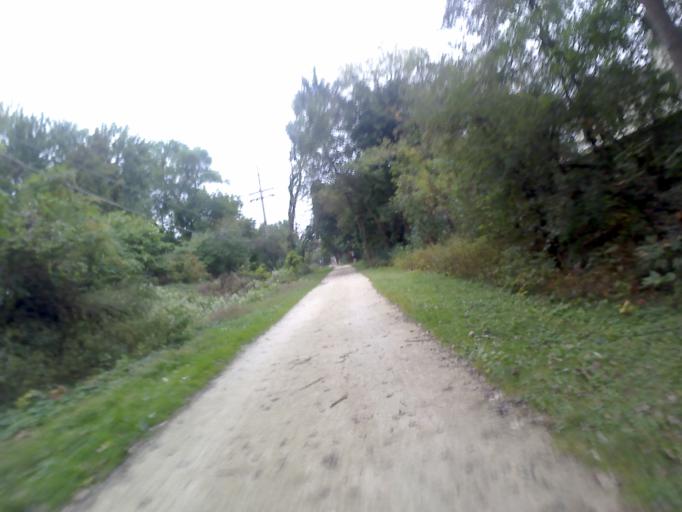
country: US
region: Illinois
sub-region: DuPage County
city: Wheaton
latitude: 41.8553
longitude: -88.1162
